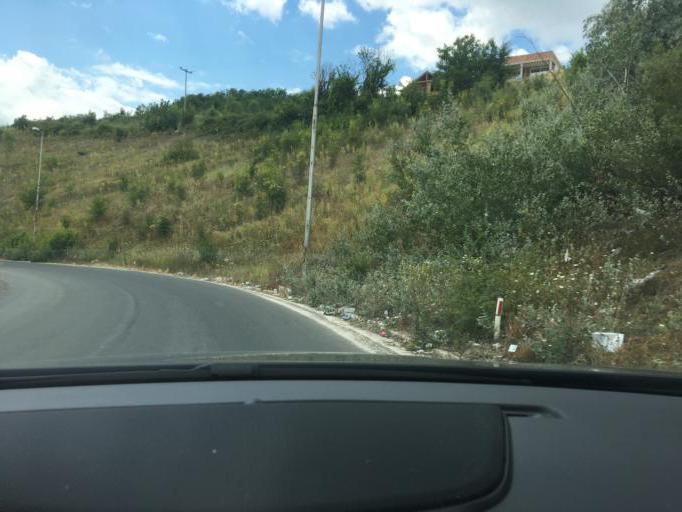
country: MK
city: Ljubin
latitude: 41.9924
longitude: 21.3118
